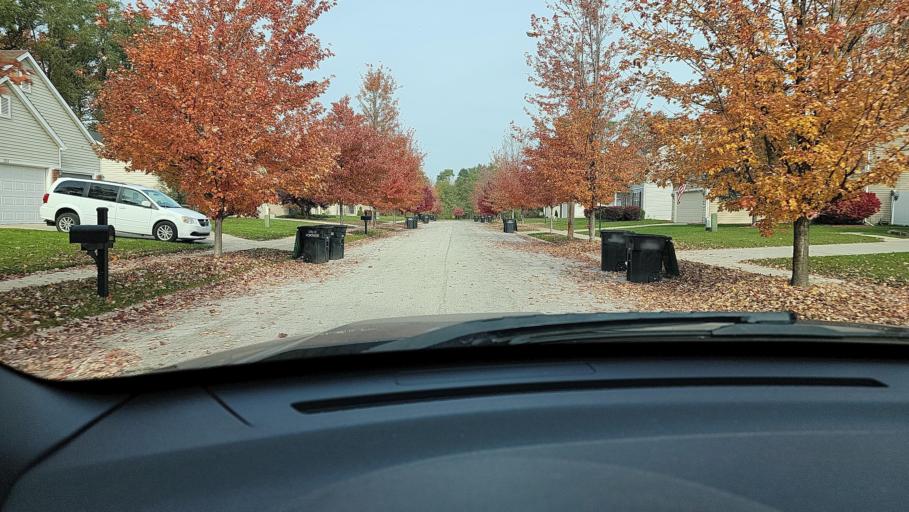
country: US
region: Indiana
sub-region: Porter County
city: Portage
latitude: 41.5958
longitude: -87.1706
